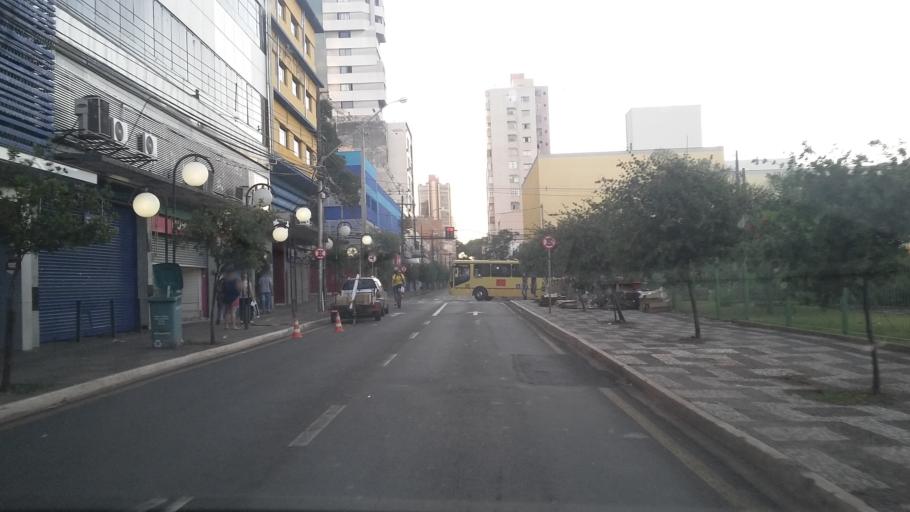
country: BR
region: Parana
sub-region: Londrina
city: Londrina
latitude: -23.3098
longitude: -51.1596
